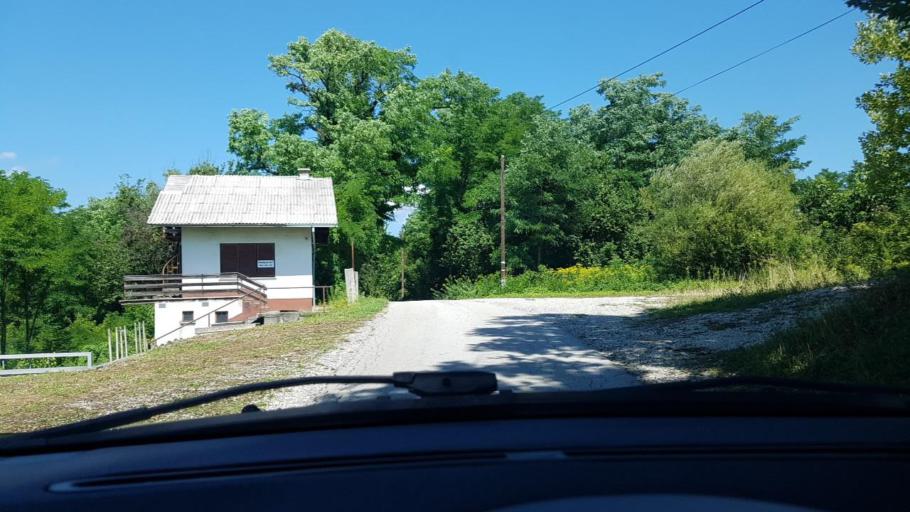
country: HR
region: Krapinsko-Zagorska
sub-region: Grad Krapina
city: Krapina
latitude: 46.1110
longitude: 15.8524
